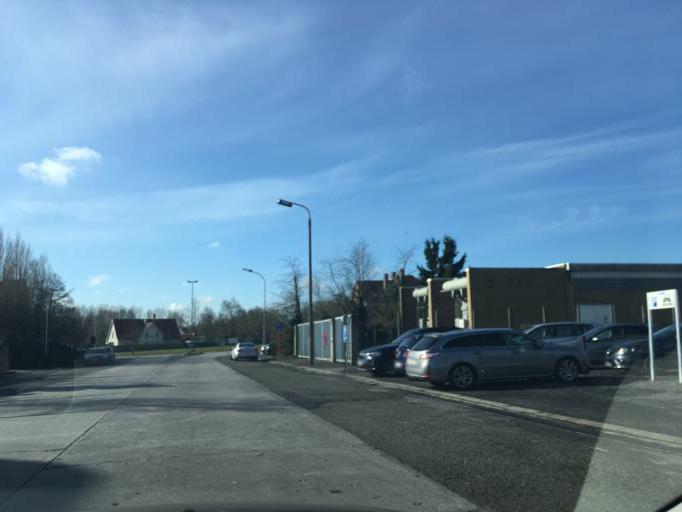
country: BE
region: Flanders
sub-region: Provincie West-Vlaanderen
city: Wevelgem
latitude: 50.8453
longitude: 3.1860
